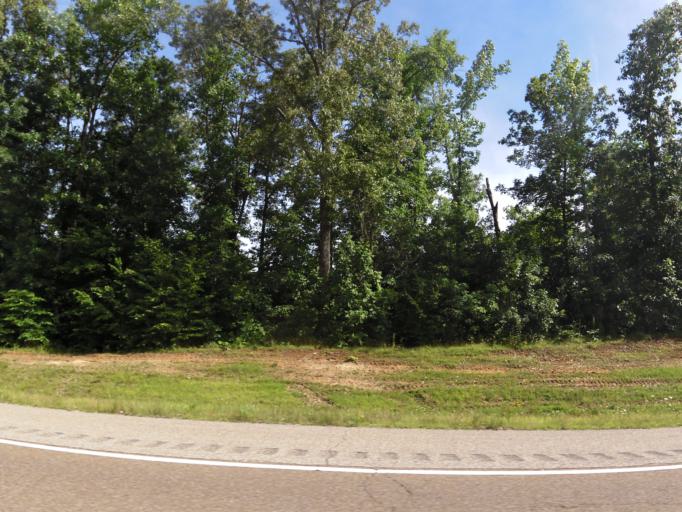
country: US
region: Tennessee
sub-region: Carroll County
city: Huntingdon
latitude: 36.0239
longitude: -88.4256
